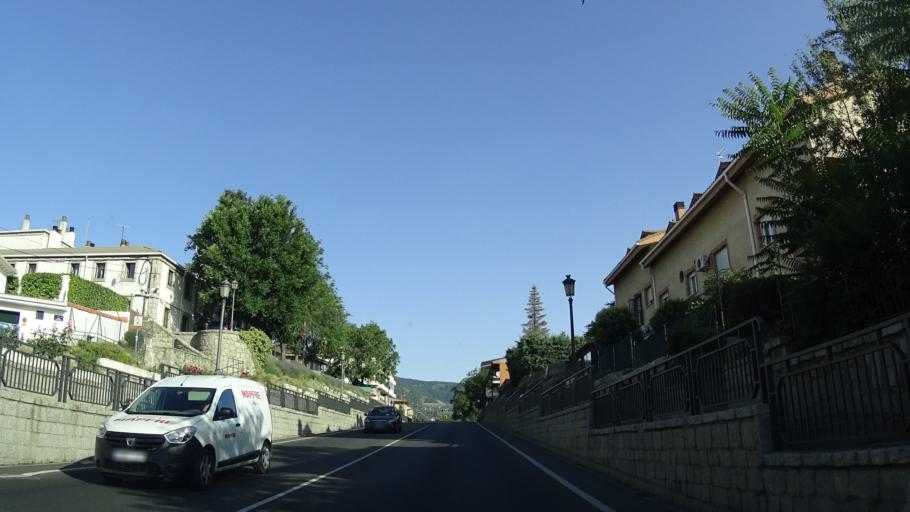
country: ES
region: Madrid
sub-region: Provincia de Madrid
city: Guadarrama
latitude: 40.6710
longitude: -4.0878
